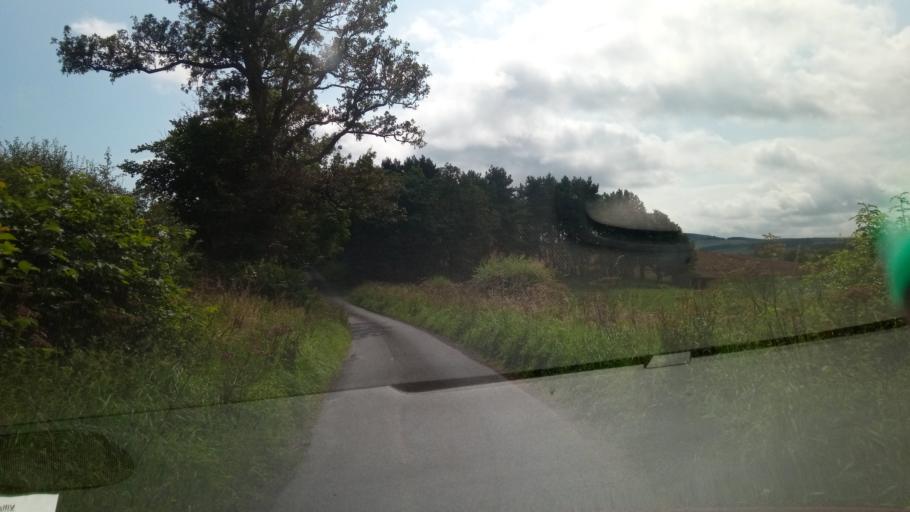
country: GB
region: Scotland
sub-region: The Scottish Borders
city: Jedburgh
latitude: 55.4675
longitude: -2.6395
